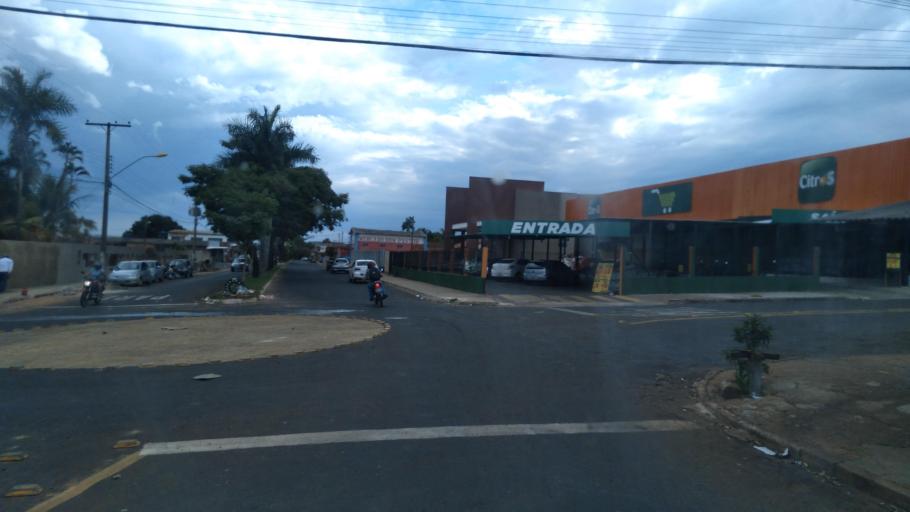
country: BR
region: Goias
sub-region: Mineiros
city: Mineiros
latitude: -17.5738
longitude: -52.5631
